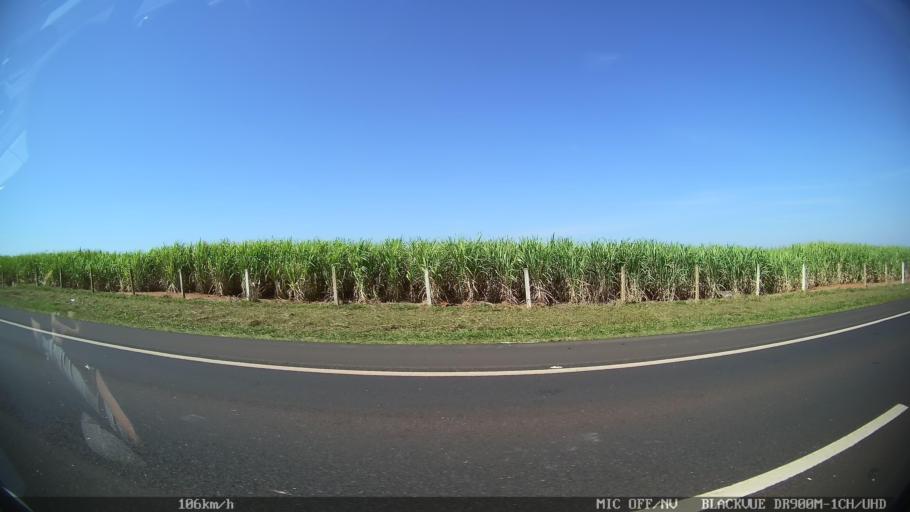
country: BR
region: Sao Paulo
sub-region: Batatais
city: Batatais
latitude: -20.8191
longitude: -47.5875
